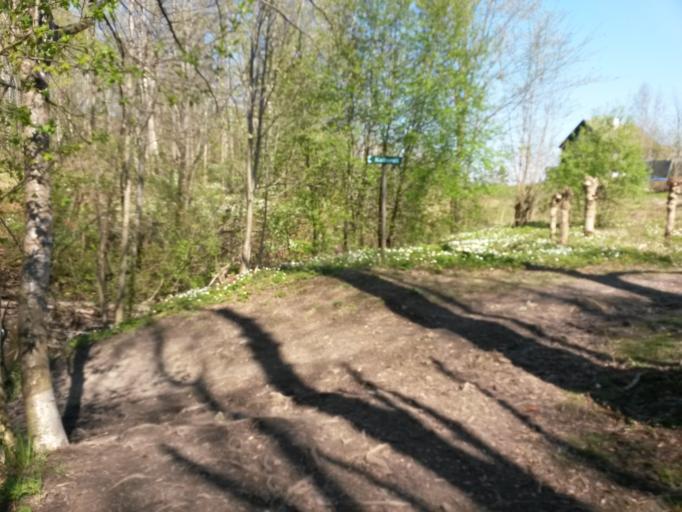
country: NO
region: Akershus
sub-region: Asker
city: Asker
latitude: 59.8340
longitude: 10.4063
